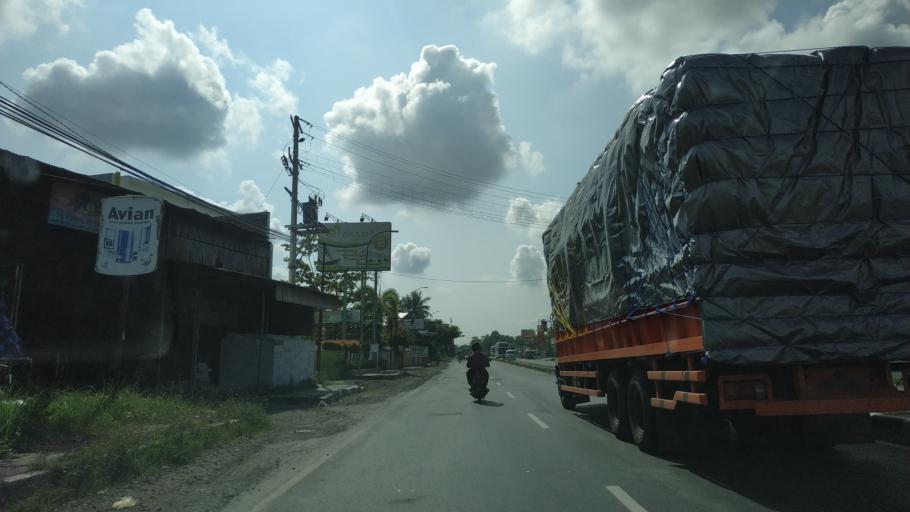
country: ID
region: Central Java
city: Comal
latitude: -6.8856
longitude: 109.5561
